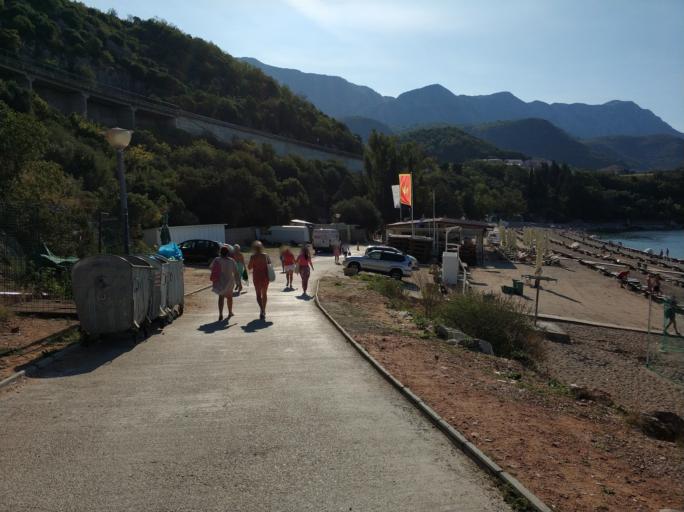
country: ME
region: Budva
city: Budva
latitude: 42.2759
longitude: 18.8863
